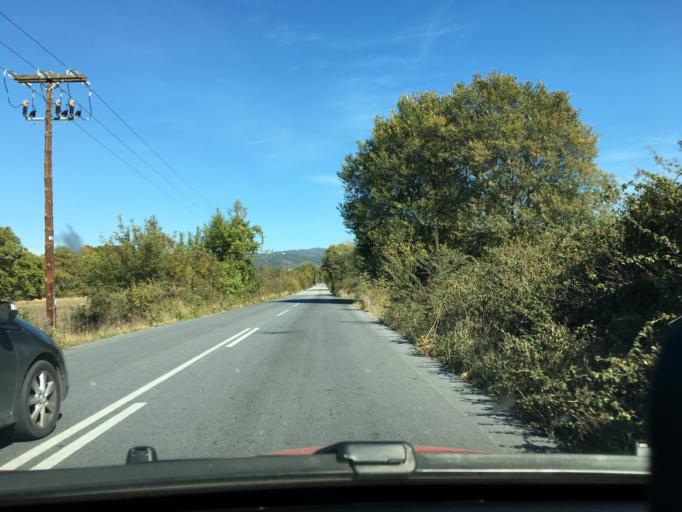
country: GR
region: Central Macedonia
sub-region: Nomos Chalkidikis
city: Megali Panagia
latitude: 40.3701
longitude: 23.6927
